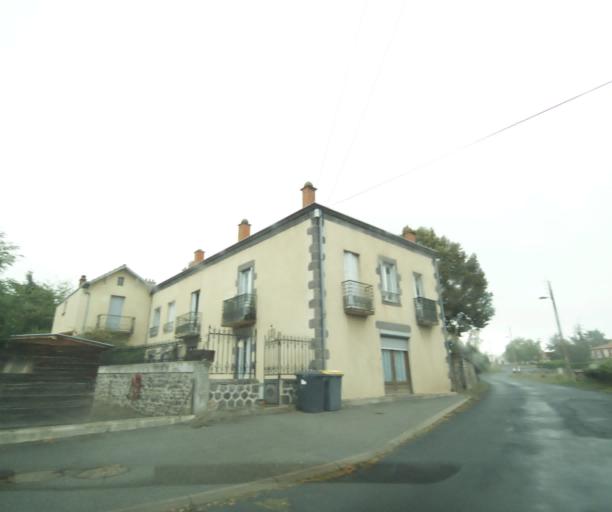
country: FR
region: Auvergne
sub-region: Departement du Puy-de-Dome
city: Chateaugay
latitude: 45.8518
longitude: 3.0852
